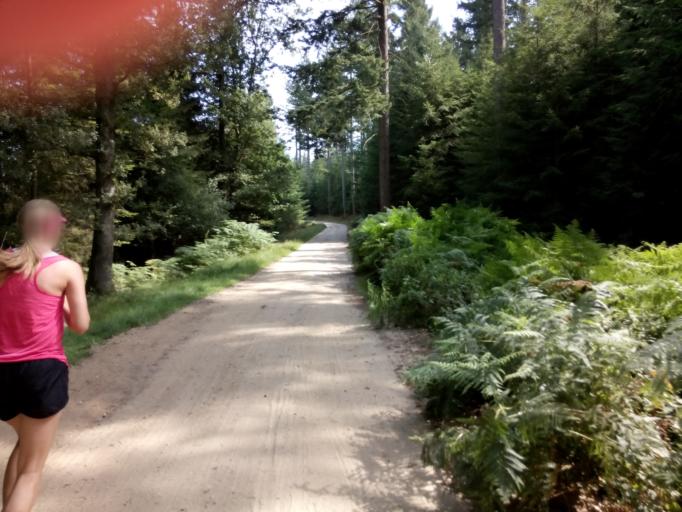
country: DK
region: Central Jutland
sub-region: Skanderborg Kommune
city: Ry
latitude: 56.0937
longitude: 9.7190
